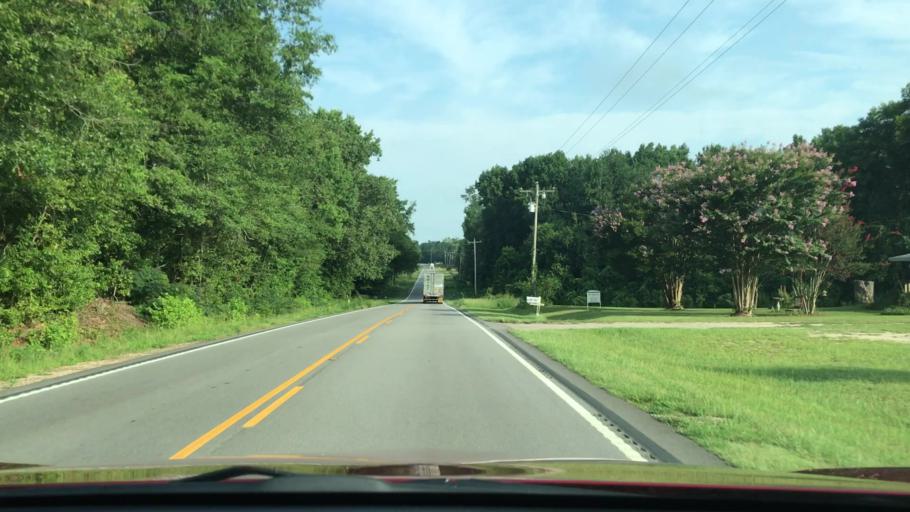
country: US
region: South Carolina
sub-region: Barnwell County
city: Blackville
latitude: 33.5561
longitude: -81.1643
